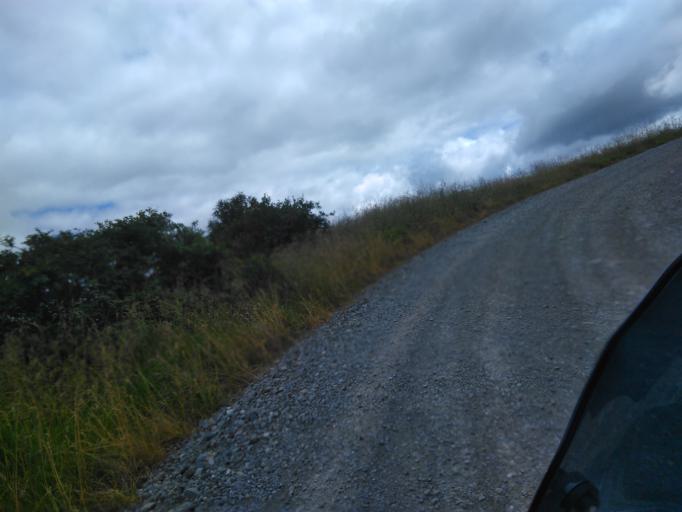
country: NZ
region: Gisborne
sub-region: Gisborne District
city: Gisborne
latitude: -38.1539
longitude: 178.1310
